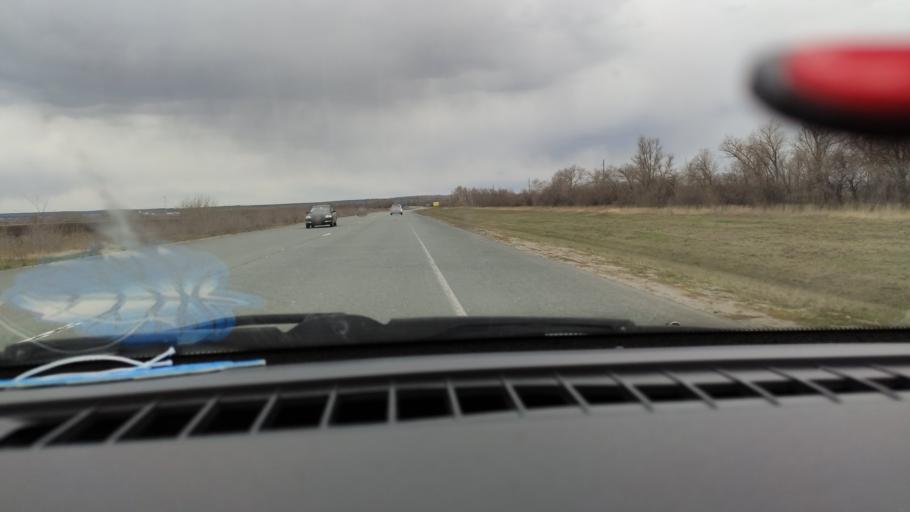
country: RU
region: Saratov
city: Yelshanka
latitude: 51.8302
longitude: 46.2412
